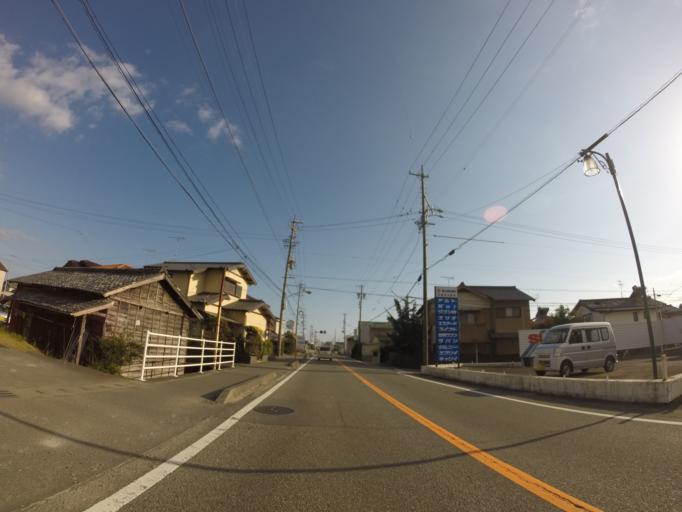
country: JP
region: Shizuoka
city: Shimada
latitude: 34.8203
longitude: 138.2114
